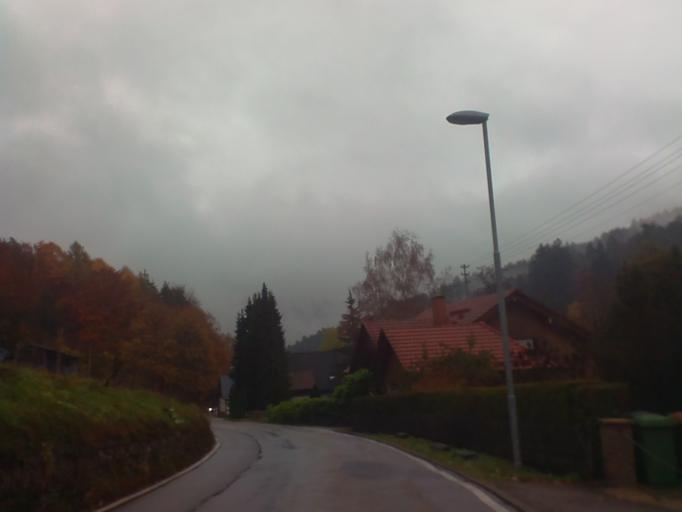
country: DE
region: Baden-Wuerttemberg
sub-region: Karlsruhe Region
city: Heiligkreuzsteinach
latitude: 49.4690
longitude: 8.7861
